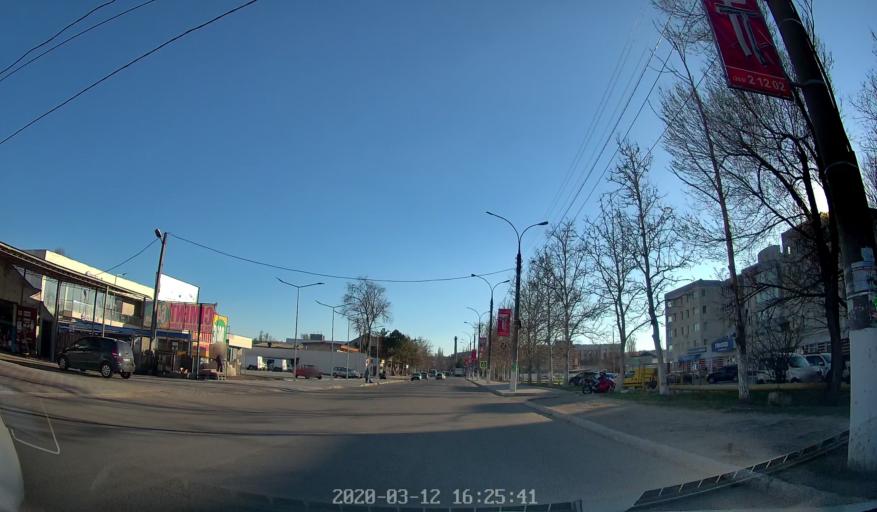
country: MD
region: Anenii Noi
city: Anenii Noi
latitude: 46.8845
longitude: 29.2341
